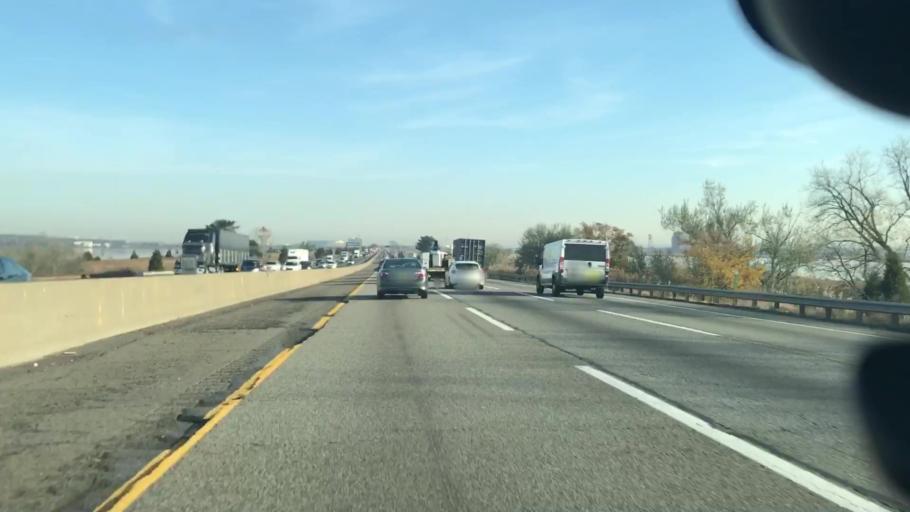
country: US
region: New Jersey
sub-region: Bergen County
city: North Arlington
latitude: 40.7638
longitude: -74.1120
